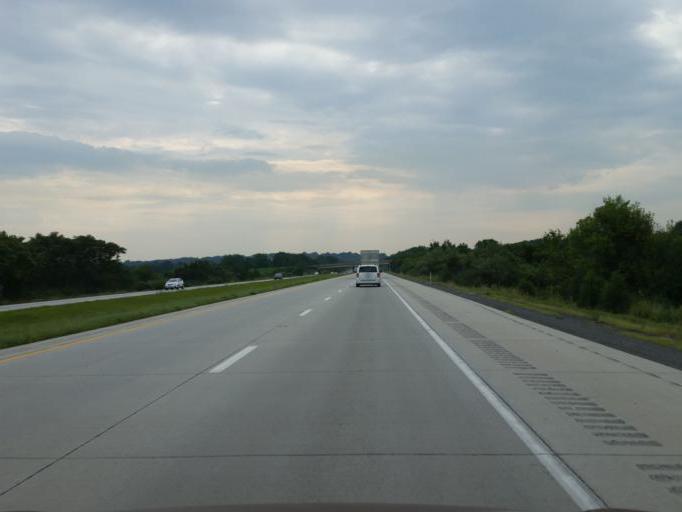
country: US
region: Pennsylvania
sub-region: Lancaster County
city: Elizabethtown
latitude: 40.1946
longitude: -76.6457
